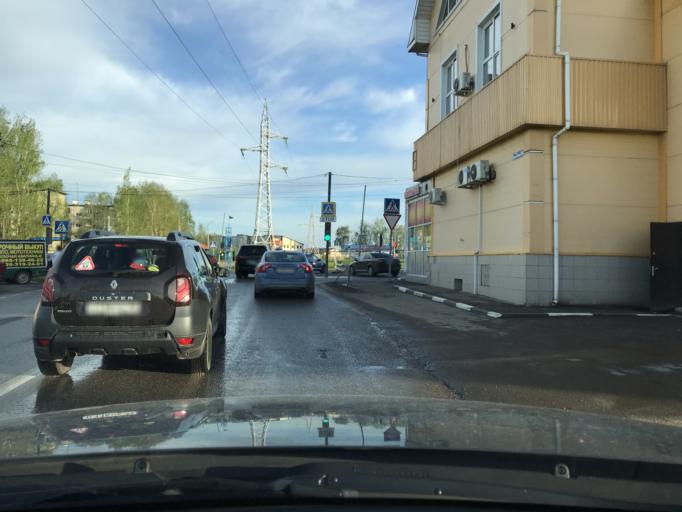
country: RU
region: Moskovskaya
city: Naro-Fominsk
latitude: 55.3794
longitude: 36.7001
